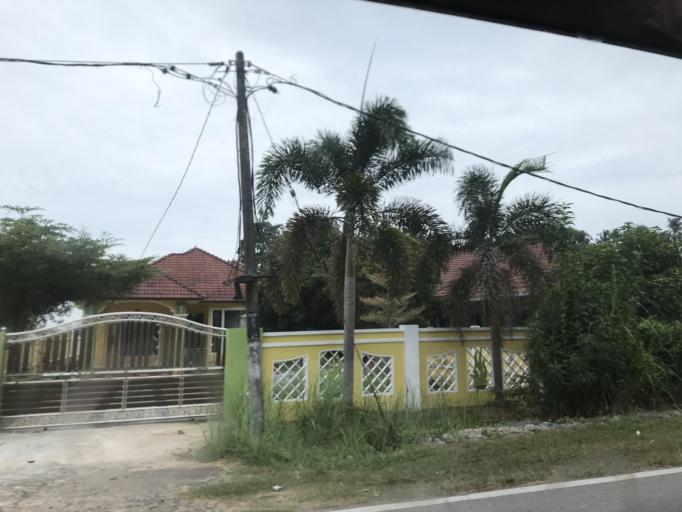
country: MY
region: Kelantan
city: Kota Bharu
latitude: 6.1479
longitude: 102.2281
